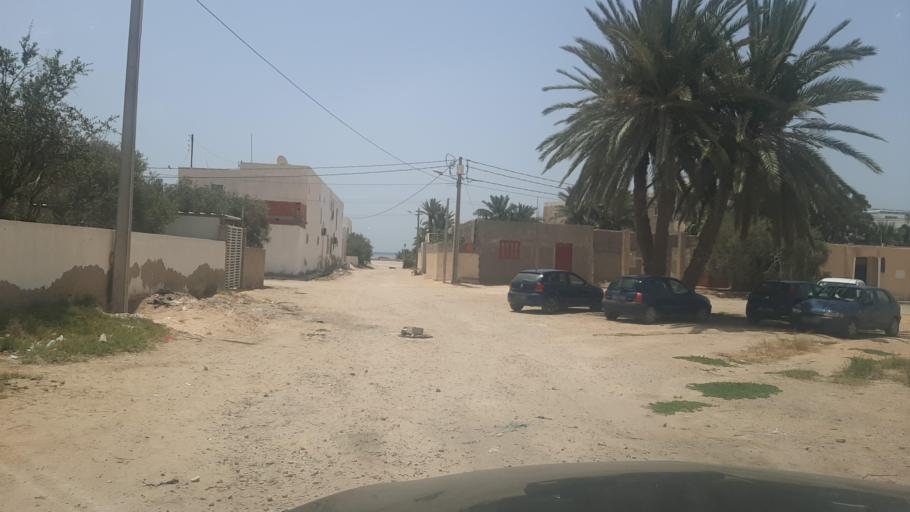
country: TN
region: Safaqis
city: Al Qarmadah
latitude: 34.7045
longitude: 11.2032
